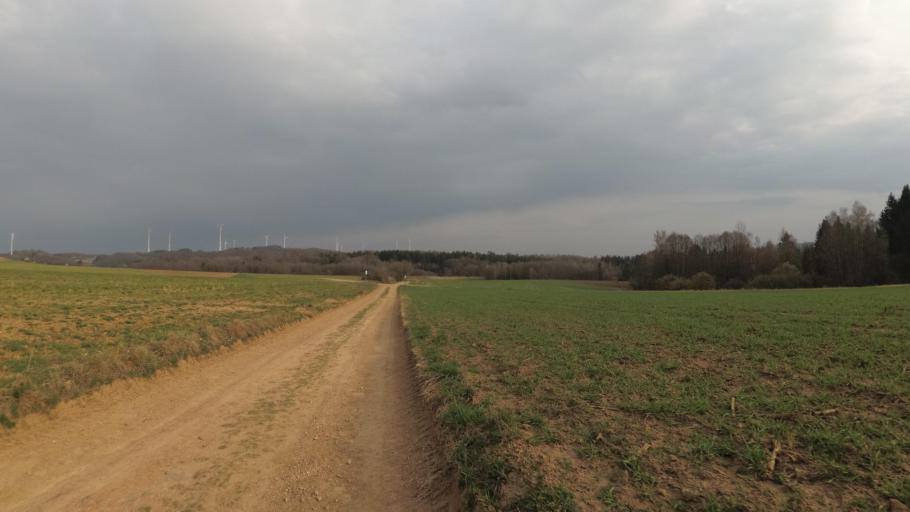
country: DE
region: Rheinland-Pfalz
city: Gimbweiler
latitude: 49.5857
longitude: 7.1727
